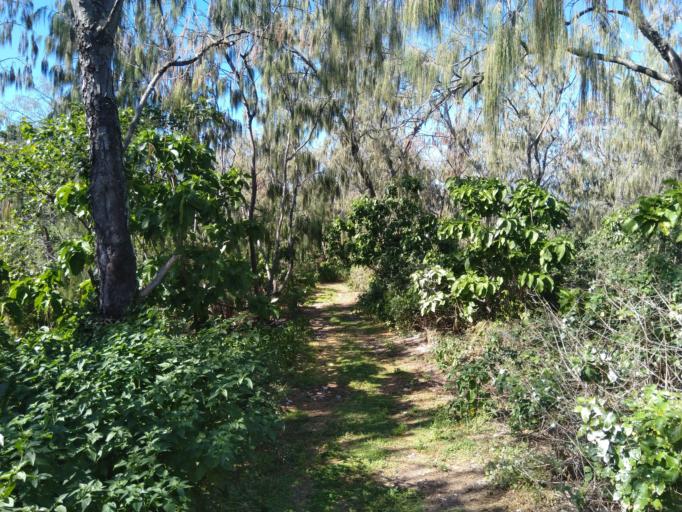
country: AU
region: Queensland
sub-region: Bundaberg
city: Bundaberg
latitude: -24.1126
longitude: 152.7130
